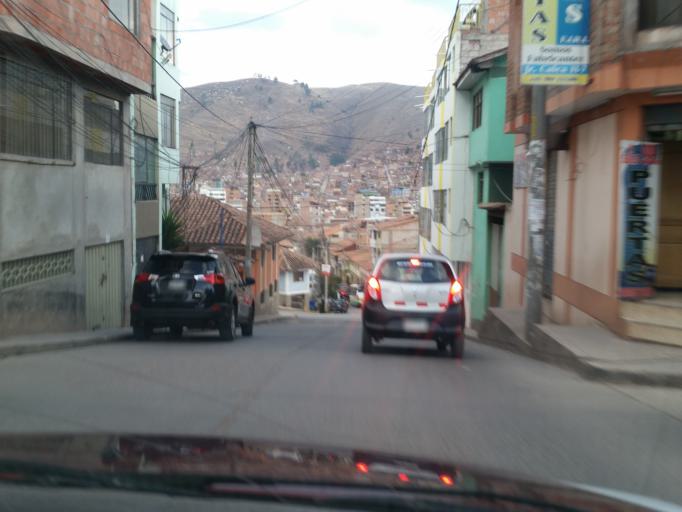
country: PE
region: Cusco
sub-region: Provincia de Cusco
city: Cusco
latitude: -13.5272
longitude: -71.9600
